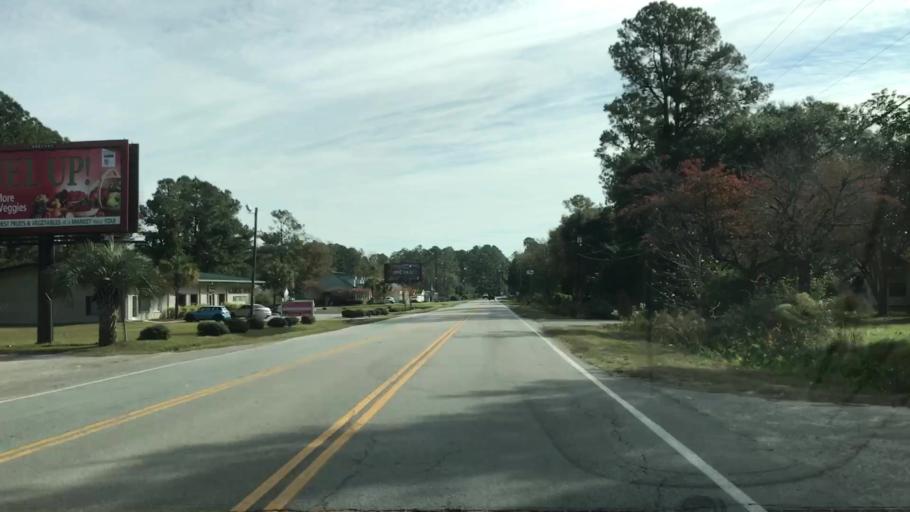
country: US
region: South Carolina
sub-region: Colleton County
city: Walterboro
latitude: 32.8957
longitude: -80.6400
